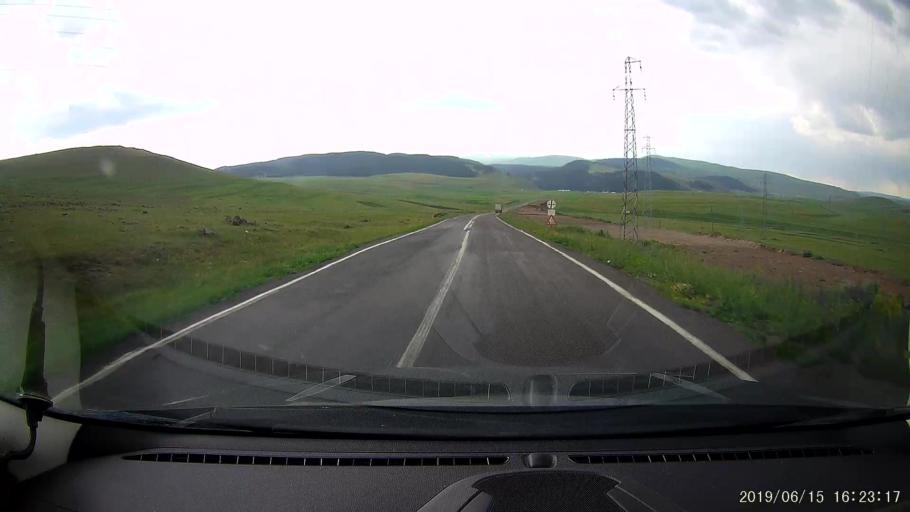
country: TR
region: Ardahan
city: Hanak
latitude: 41.1796
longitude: 42.8606
